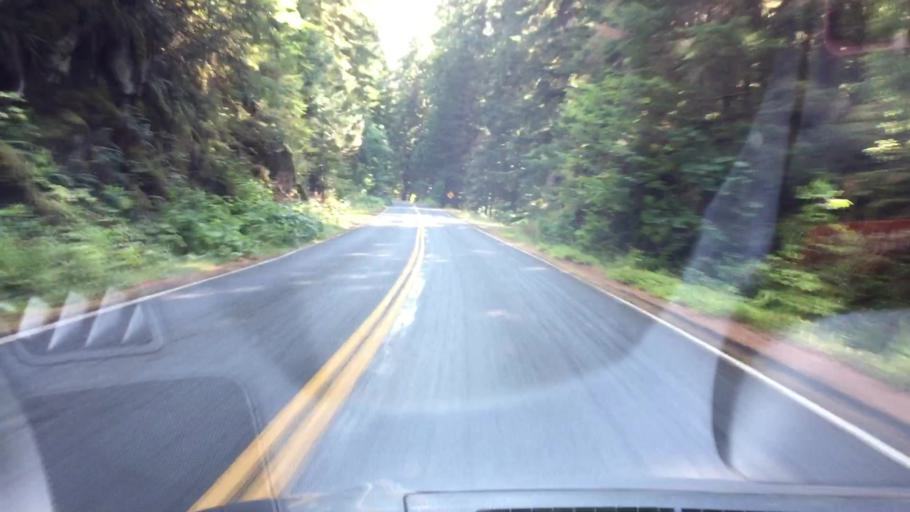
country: US
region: Washington
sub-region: Pierce County
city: Buckley
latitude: 46.7352
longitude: -121.5659
